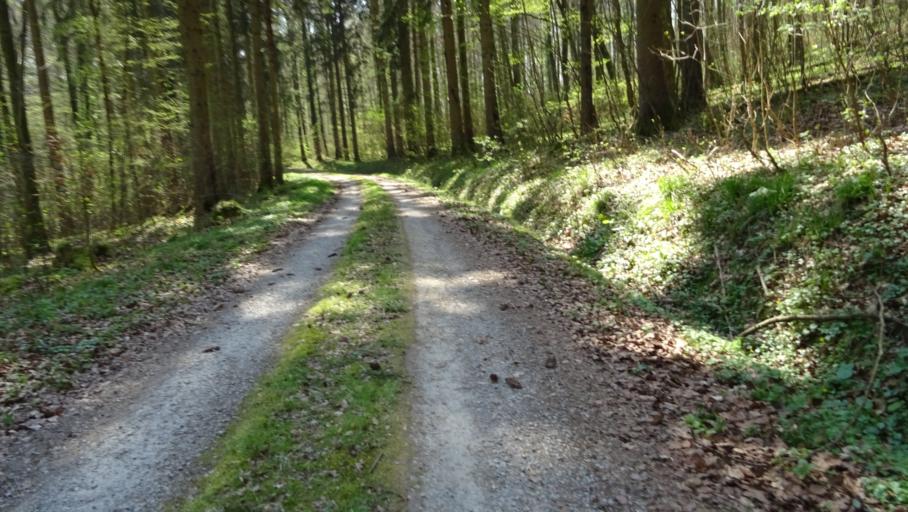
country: DE
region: Baden-Wuerttemberg
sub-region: Karlsruhe Region
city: Obrigheim
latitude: 49.3730
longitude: 9.1023
